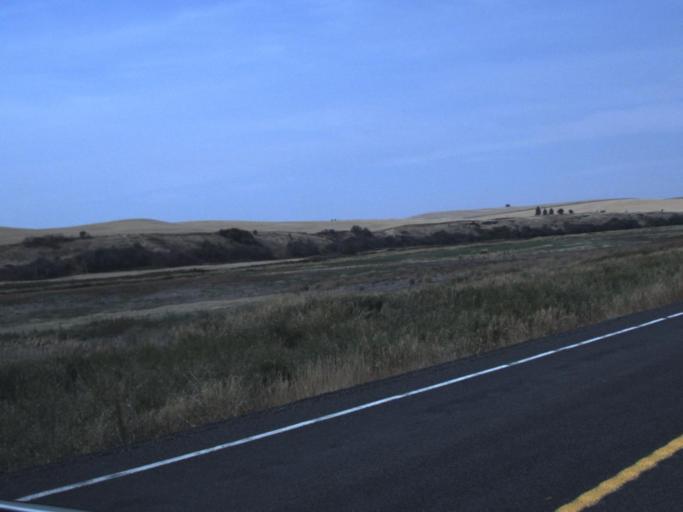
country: US
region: Idaho
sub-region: Benewah County
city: Plummer
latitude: 47.3184
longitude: -117.1745
